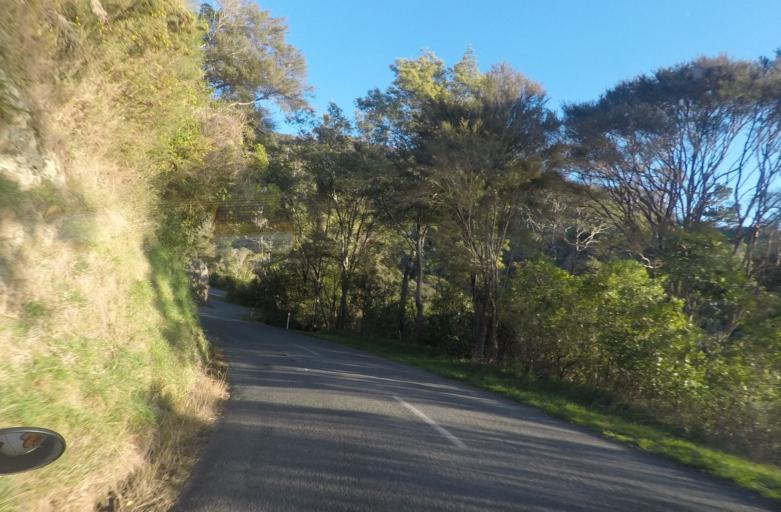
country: NZ
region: Marlborough
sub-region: Marlborough District
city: Picton
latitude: -41.2697
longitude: 173.9524
